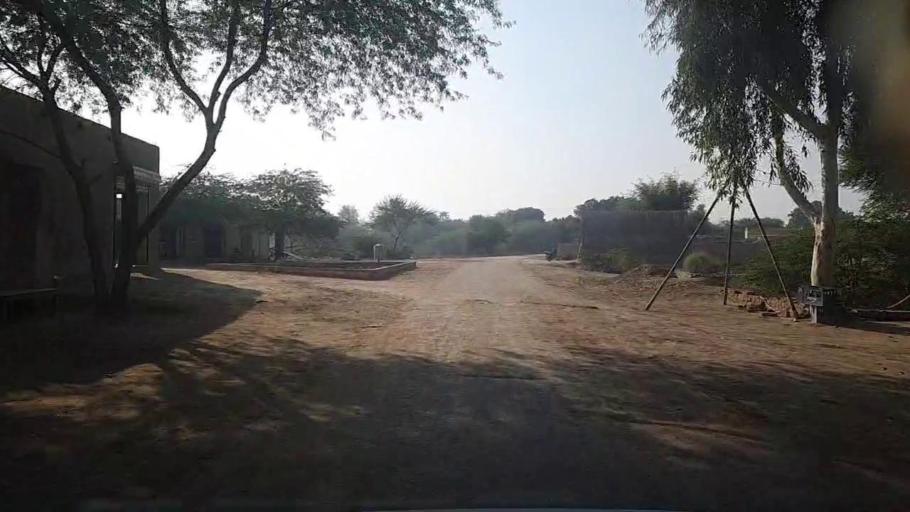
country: PK
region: Sindh
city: Karaundi
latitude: 26.7877
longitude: 68.4689
